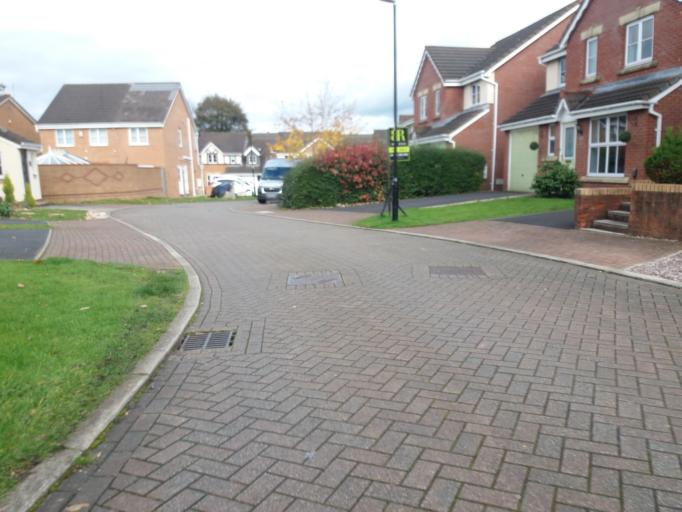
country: GB
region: England
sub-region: Lancashire
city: Chorley
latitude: 53.6463
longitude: -2.6229
